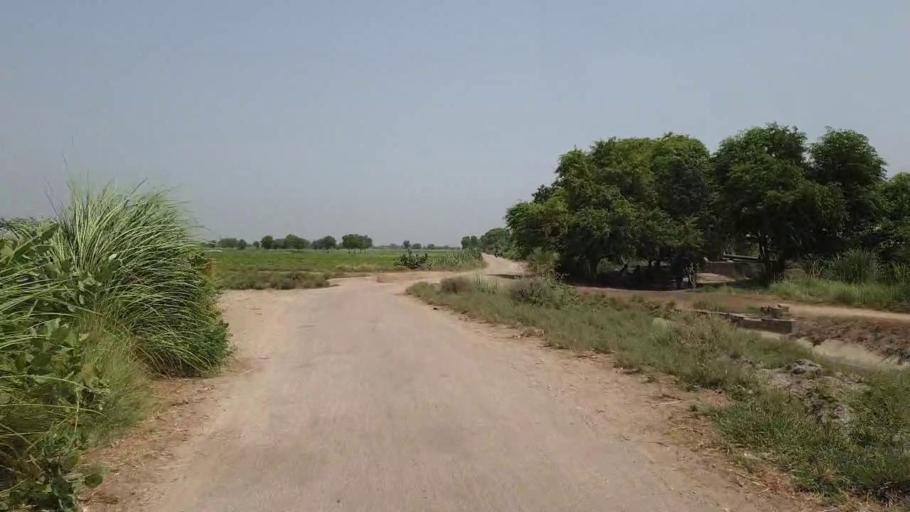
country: PK
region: Sindh
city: Nawabshah
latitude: 26.2876
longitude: 68.3095
